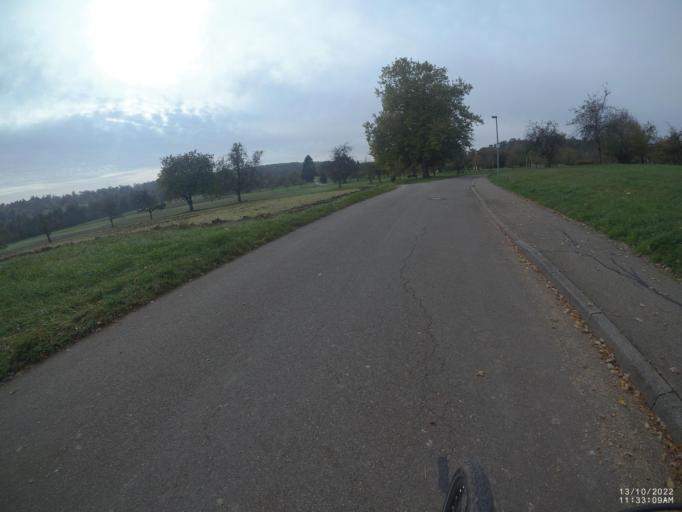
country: DE
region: Baden-Wuerttemberg
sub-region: Regierungsbezirk Stuttgart
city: Schlierbach
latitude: 48.6679
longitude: 9.5203
